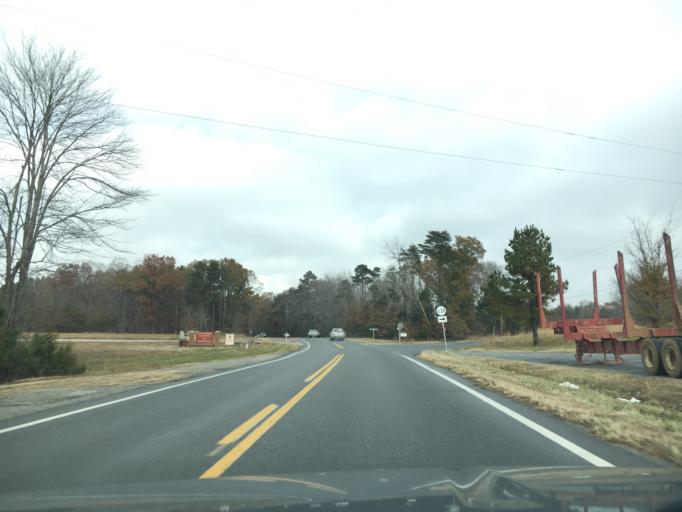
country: US
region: Virginia
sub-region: Prince Edward County
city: Farmville
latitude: 37.3685
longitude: -78.3704
